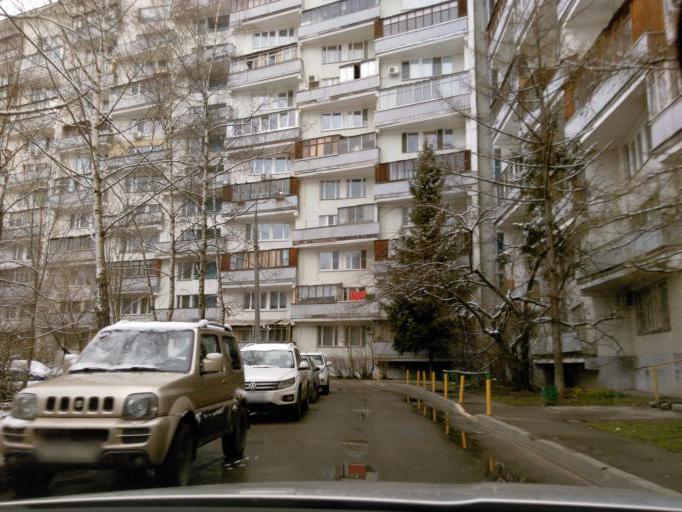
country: RU
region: Moskovskaya
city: Mendeleyevo
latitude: 56.0110
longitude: 37.2076
